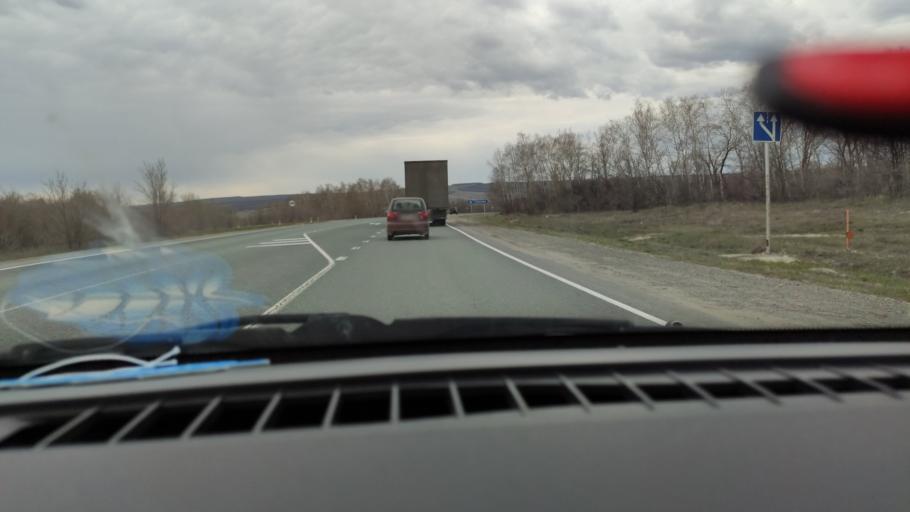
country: RU
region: Saratov
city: Sinodskoye
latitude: 51.9334
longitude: 46.5854
